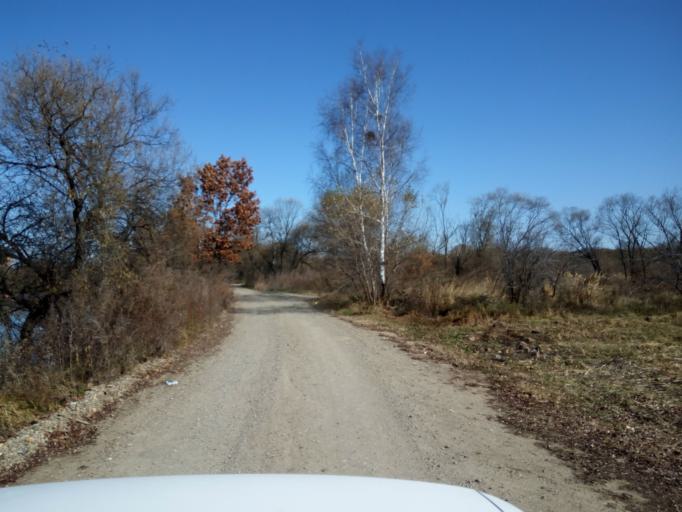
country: RU
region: Primorskiy
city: Dal'nerechensk
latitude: 45.9171
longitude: 133.7881
